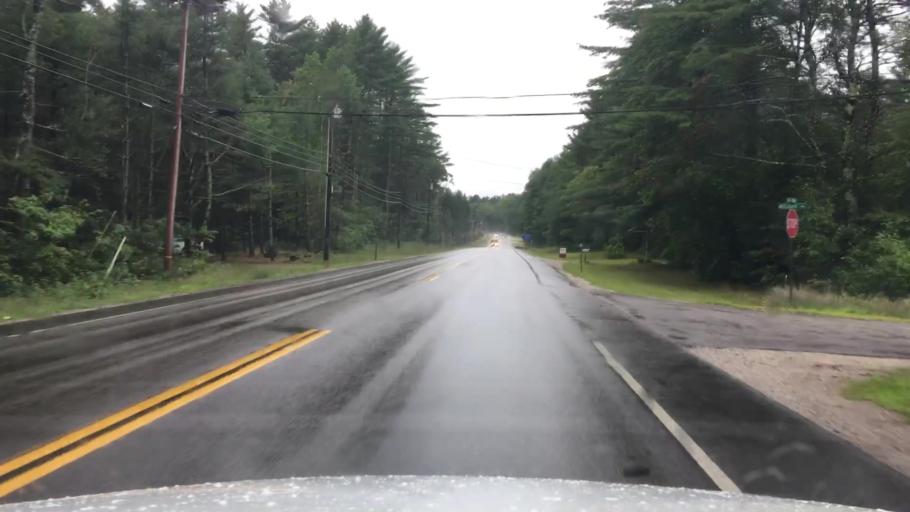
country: US
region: Maine
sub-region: Oxford County
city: Fryeburg
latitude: 43.9982
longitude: -71.0181
